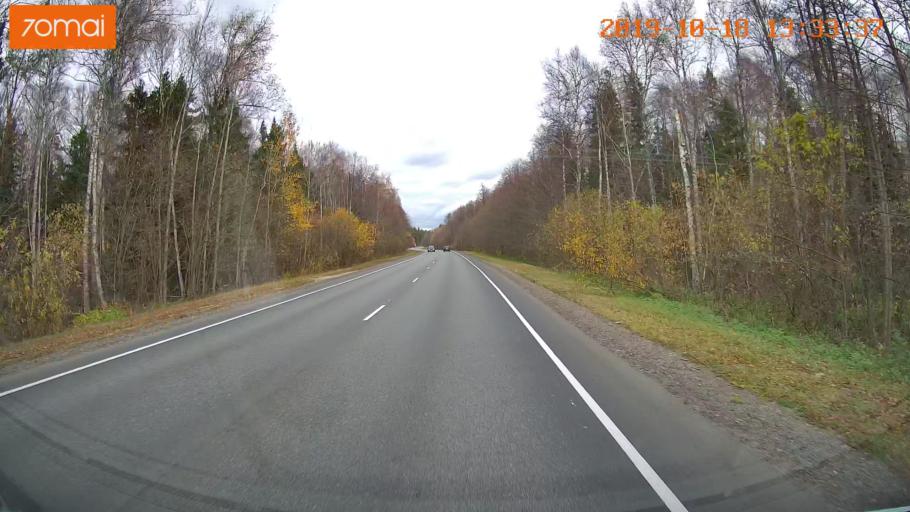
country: RU
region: Rjazan
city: Solotcha
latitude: 54.8453
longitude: 39.9398
